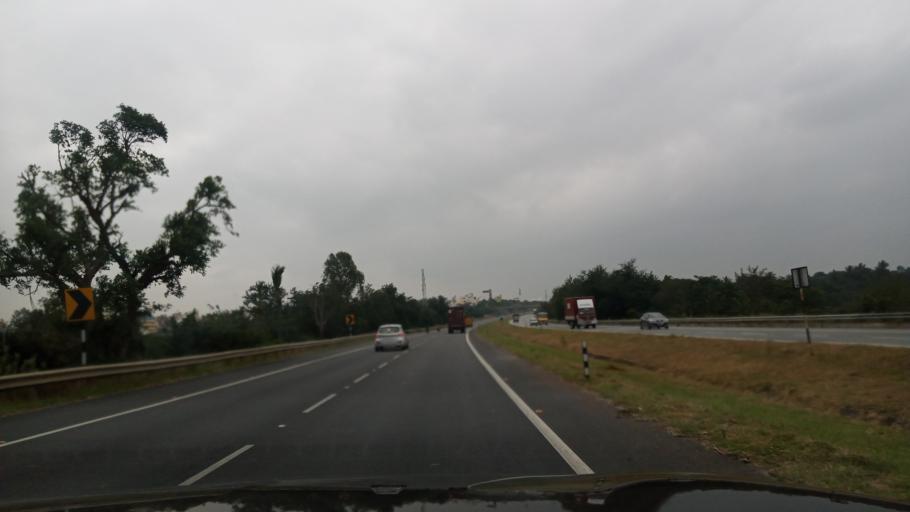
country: IN
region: Karnataka
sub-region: Bangalore Rural
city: Nelamangala
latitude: 13.0187
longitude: 77.4761
